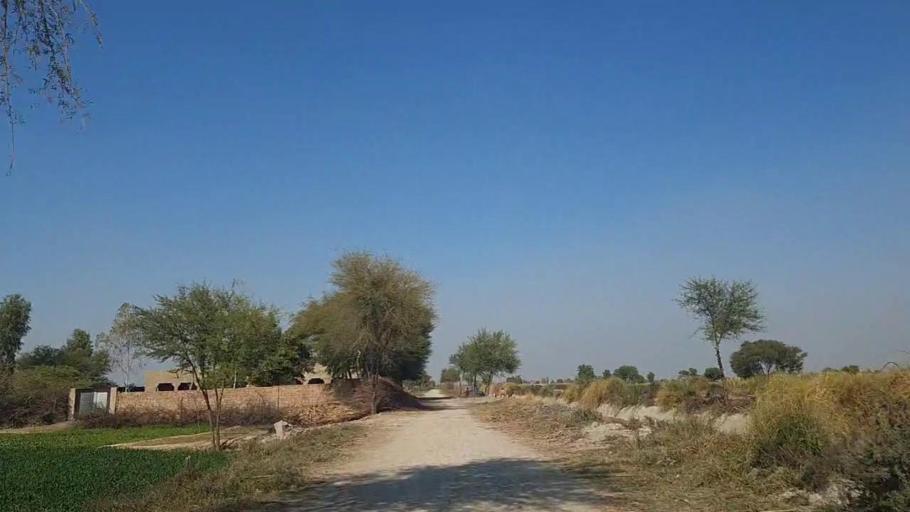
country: PK
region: Sindh
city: Sakrand
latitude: 26.2666
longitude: 68.2210
